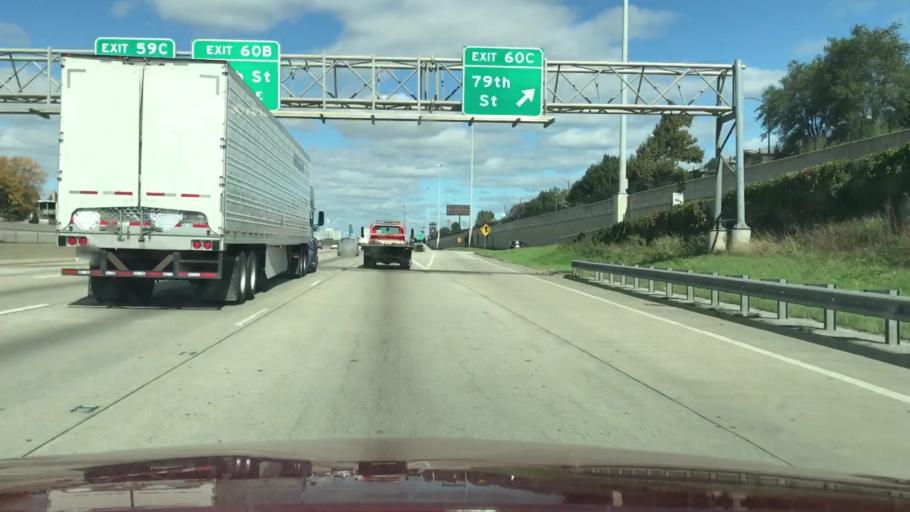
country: US
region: Illinois
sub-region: Cook County
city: Evergreen Park
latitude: 41.7447
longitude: -87.6248
